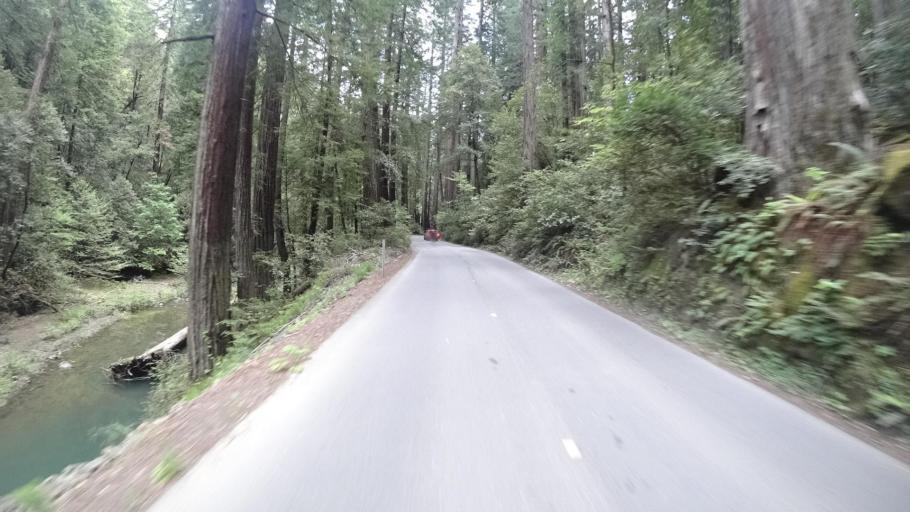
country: US
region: California
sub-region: Humboldt County
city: Redway
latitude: 40.1232
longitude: -123.8437
